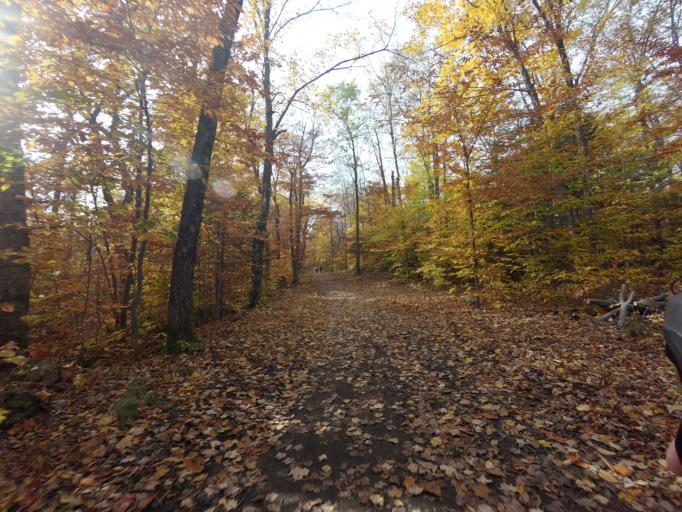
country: CA
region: Quebec
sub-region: Outaouais
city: Wakefield
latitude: 45.5065
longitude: -75.8952
